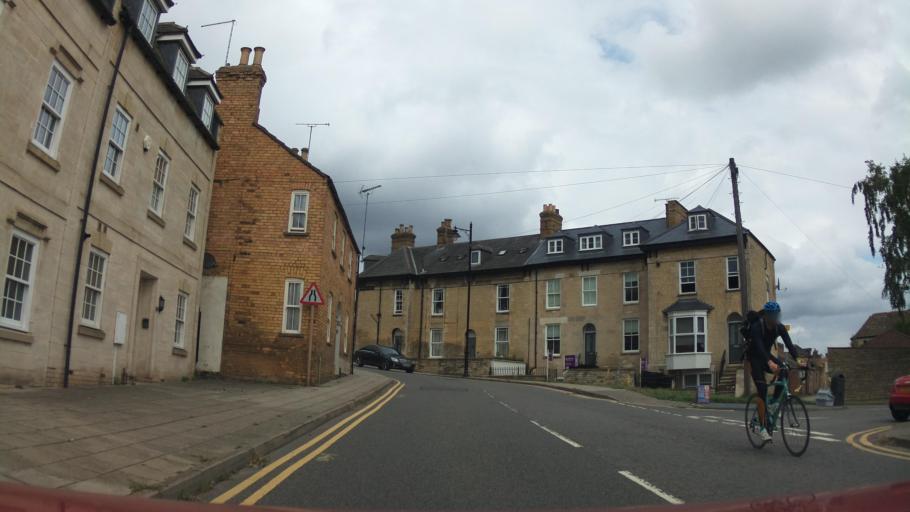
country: GB
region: England
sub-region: Lincolnshire
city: Stamford
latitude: 52.6525
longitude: -0.4731
